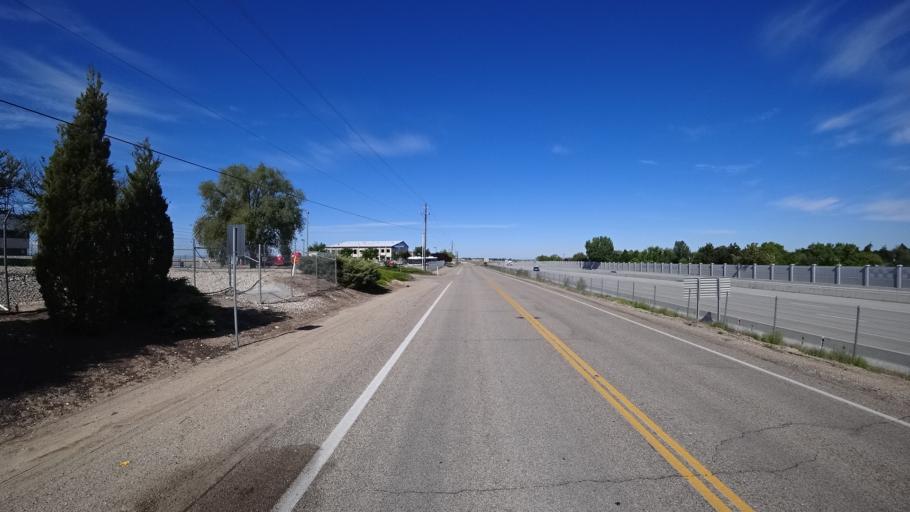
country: US
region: Idaho
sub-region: Ada County
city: Boise
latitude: 43.5717
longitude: -116.2301
